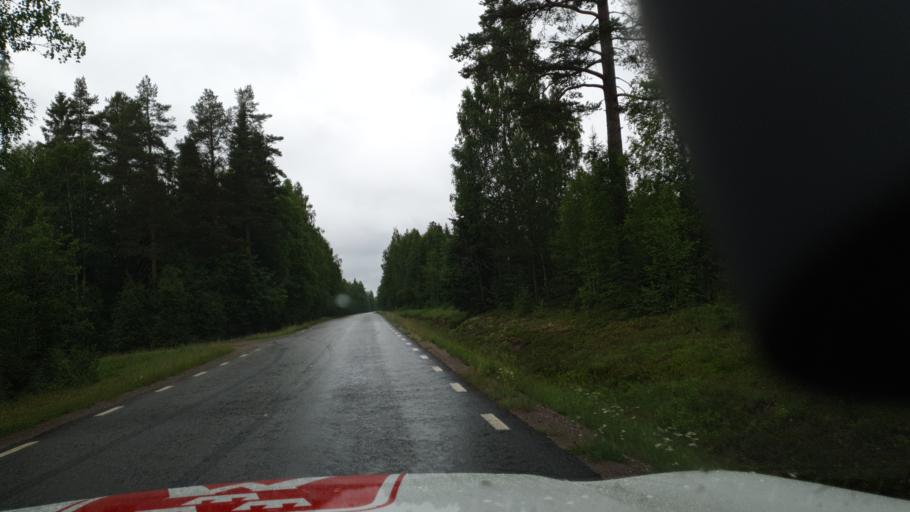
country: SE
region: Vaesterbotten
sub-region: Vannas Kommun
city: Vannasby
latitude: 63.8190
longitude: 19.8563
